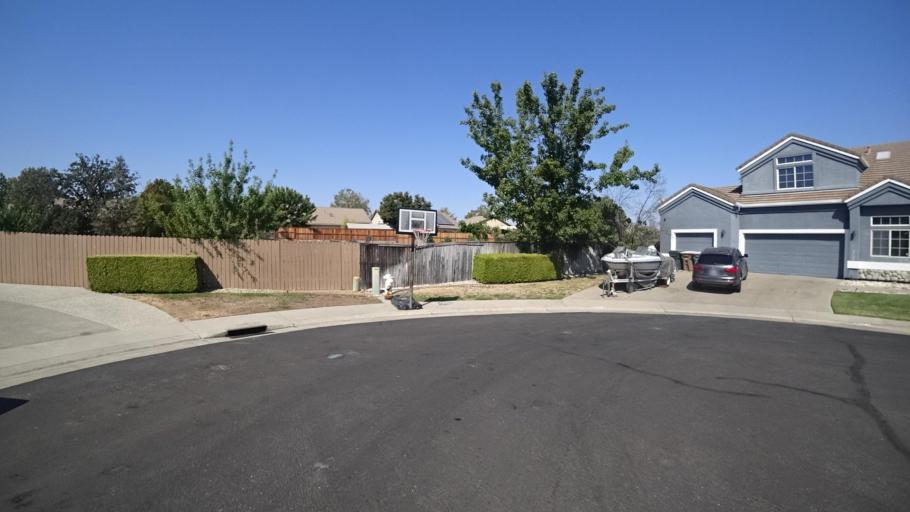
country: US
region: California
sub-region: Sacramento County
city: Vineyard
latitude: 38.4505
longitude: -121.3887
